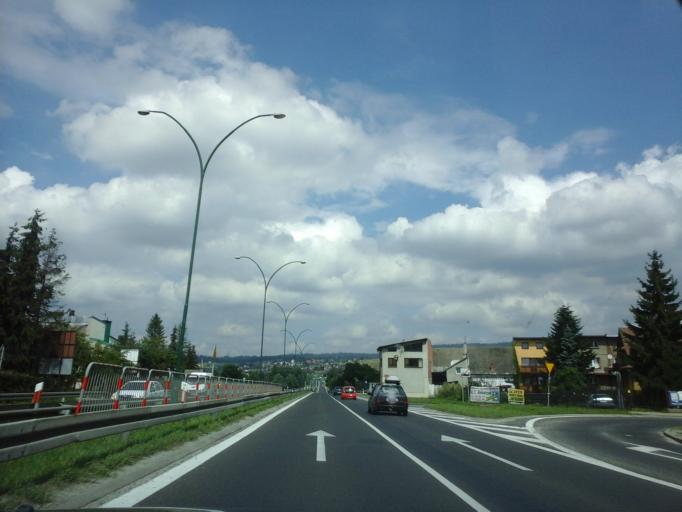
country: PL
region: Lesser Poland Voivodeship
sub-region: Powiat nowotarski
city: Nowy Targ
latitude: 49.4792
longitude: 20.0219
